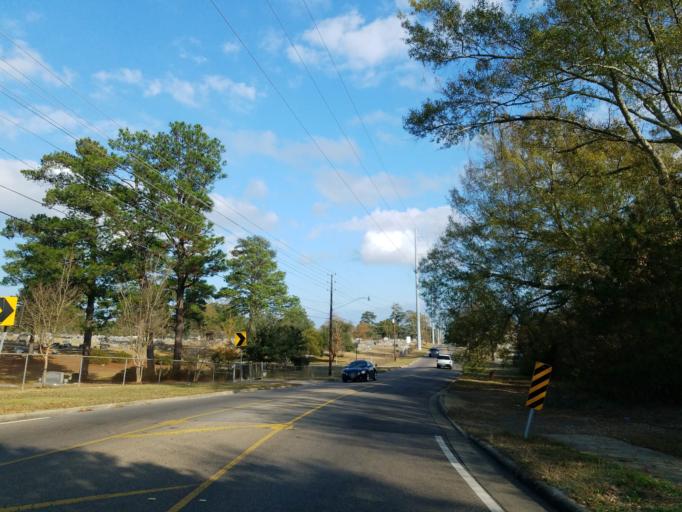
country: US
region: Mississippi
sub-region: Lamar County
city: Arnold Line
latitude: 31.3359
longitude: -89.3438
